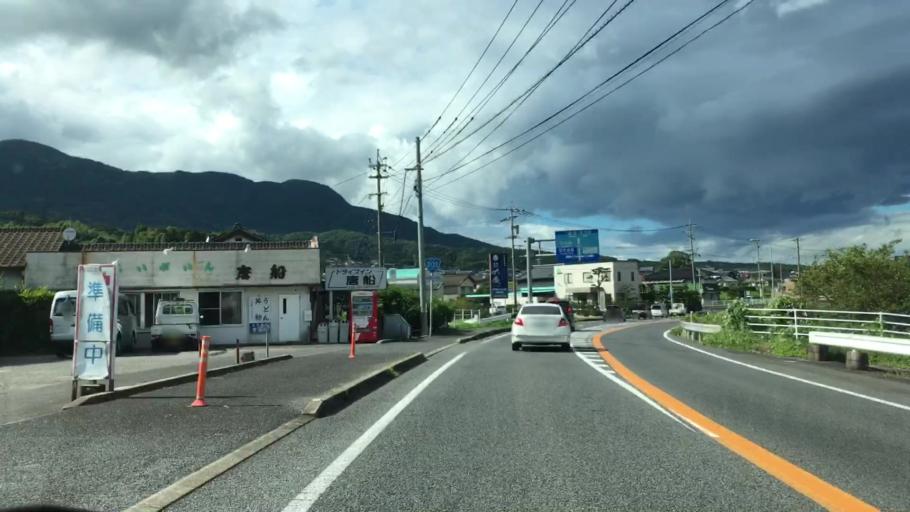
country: JP
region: Saga Prefecture
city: Imaricho-ko
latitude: 33.2242
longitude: 129.8473
